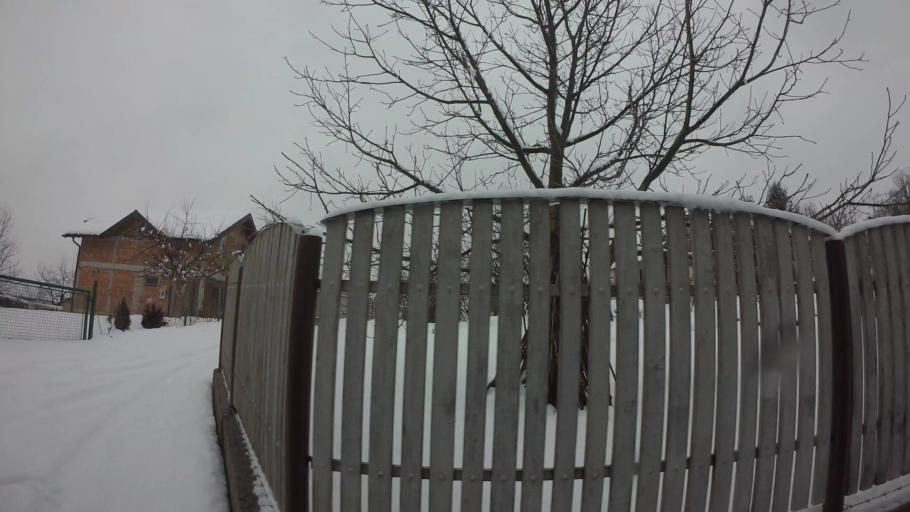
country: BA
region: Federation of Bosnia and Herzegovina
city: Hadzici
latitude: 43.8595
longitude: 18.2610
